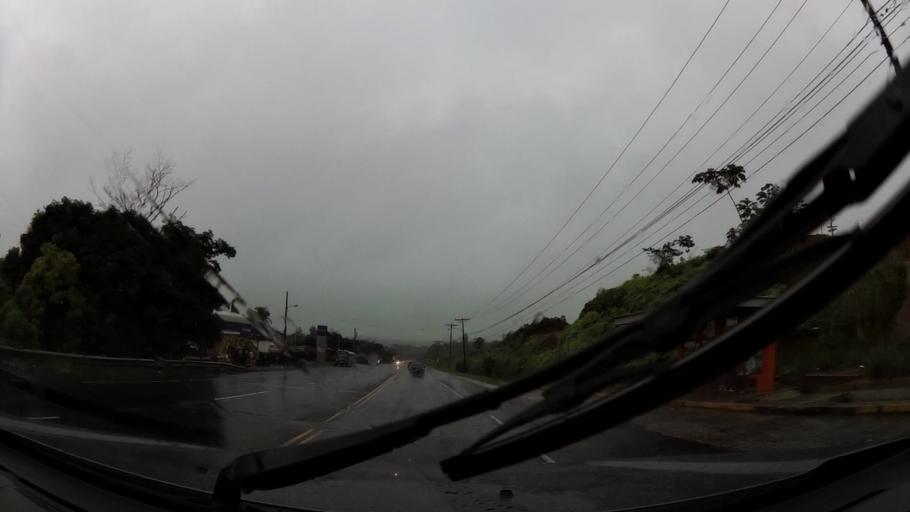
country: PA
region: Colon
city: Rio Rita
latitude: 9.3166
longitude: -79.7937
